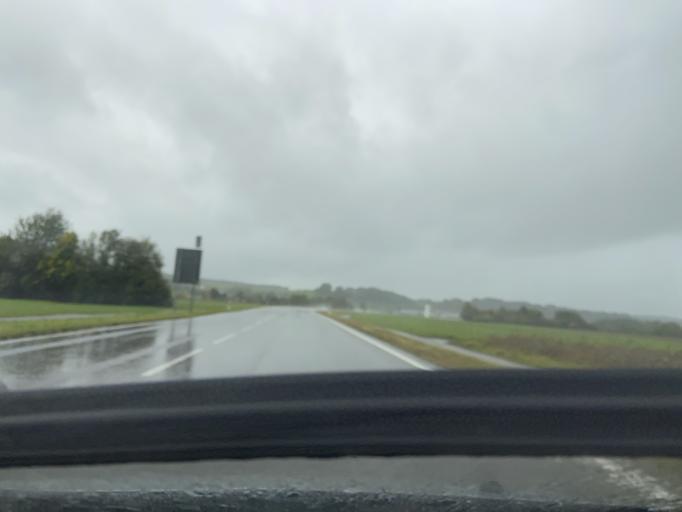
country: DE
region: Baden-Wuerttemberg
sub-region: Tuebingen Region
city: Ennetach
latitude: 48.0574
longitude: 9.3132
